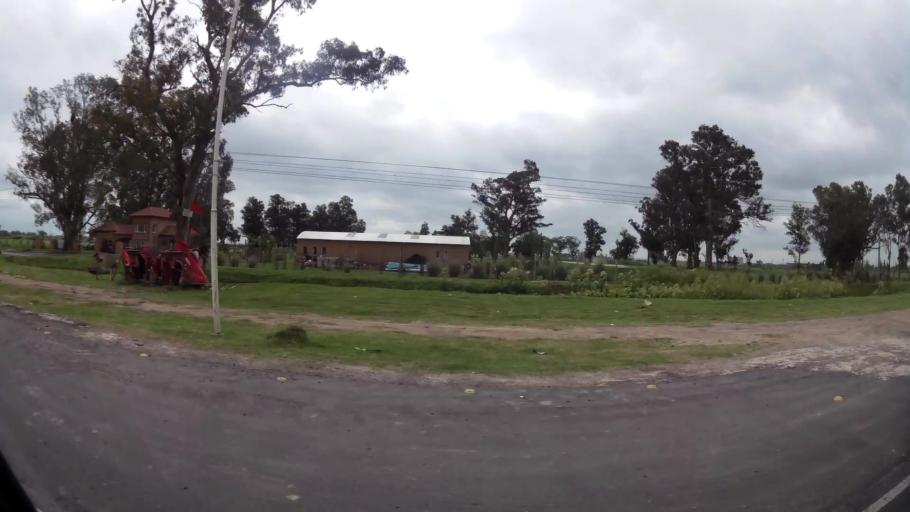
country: AR
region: Buenos Aires
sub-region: Partido de San Vicente
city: San Vicente
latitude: -34.9750
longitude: -58.4677
